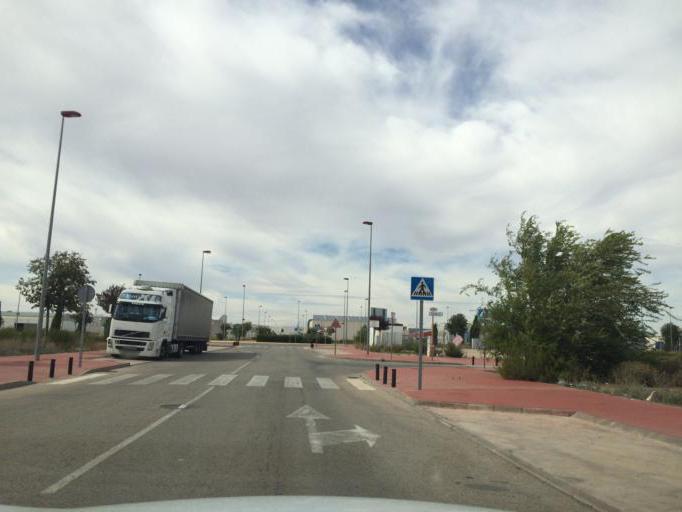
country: ES
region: Castille-La Mancha
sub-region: Provincia de Albacete
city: Albacete
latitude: 39.0256
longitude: -1.8862
